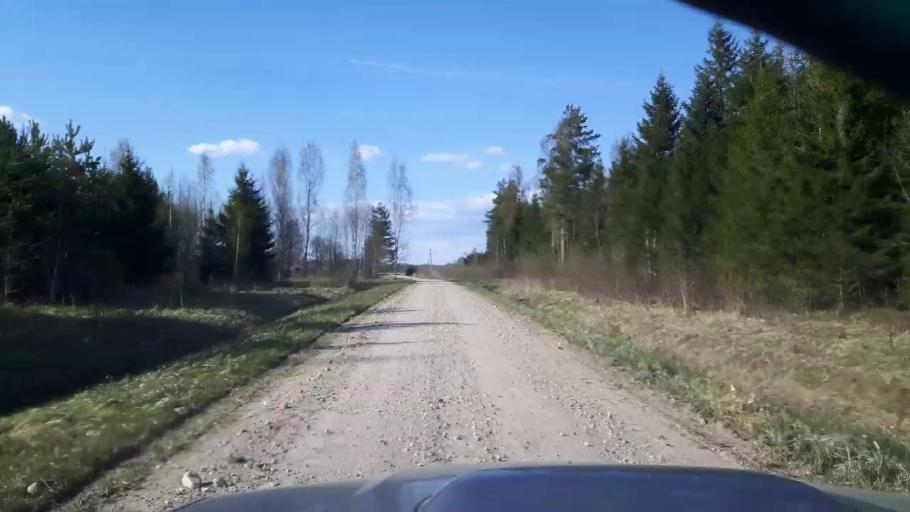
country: EE
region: Paernumaa
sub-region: Tootsi vald
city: Tootsi
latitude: 58.4302
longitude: 24.8509
